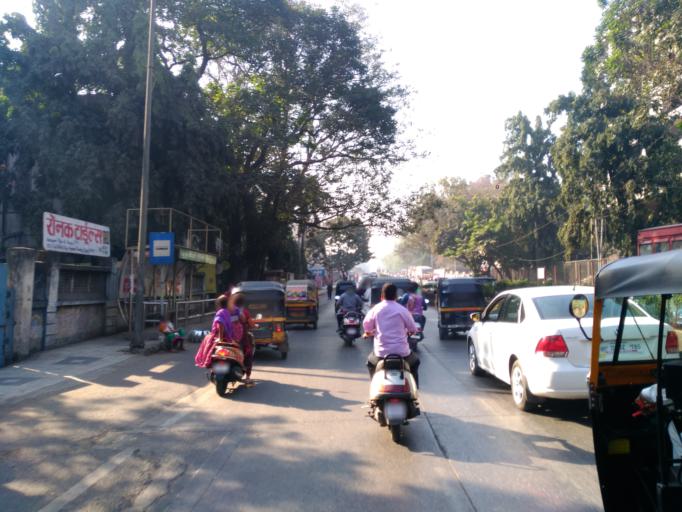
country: IN
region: Maharashtra
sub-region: Pune Division
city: Pune
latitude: 18.5004
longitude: 73.8695
